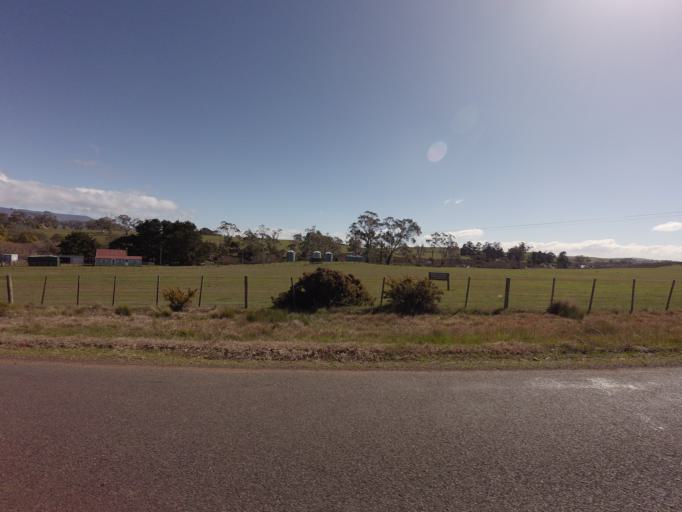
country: AU
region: Tasmania
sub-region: Northern Midlands
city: Evandale
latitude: -41.9066
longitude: 147.3933
